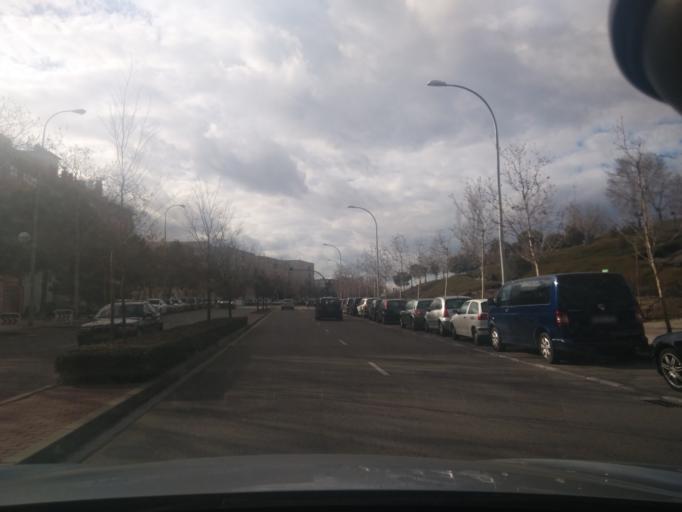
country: ES
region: Madrid
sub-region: Provincia de Madrid
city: Alcobendas
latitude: 40.5474
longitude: -3.6578
